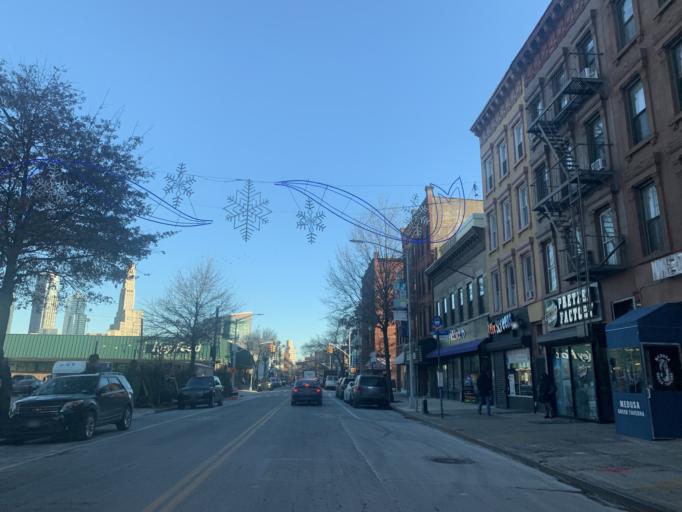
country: US
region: New York
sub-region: Kings County
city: Brooklyn
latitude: 40.6785
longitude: -73.9790
